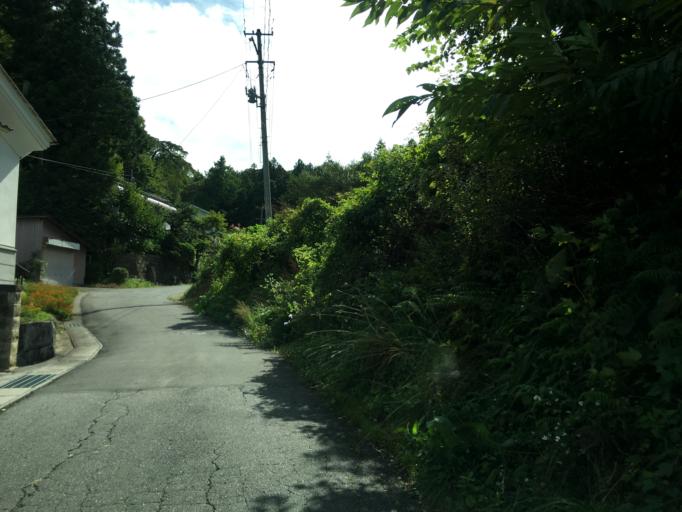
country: JP
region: Fukushima
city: Ishikawa
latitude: 37.2403
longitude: 140.5720
